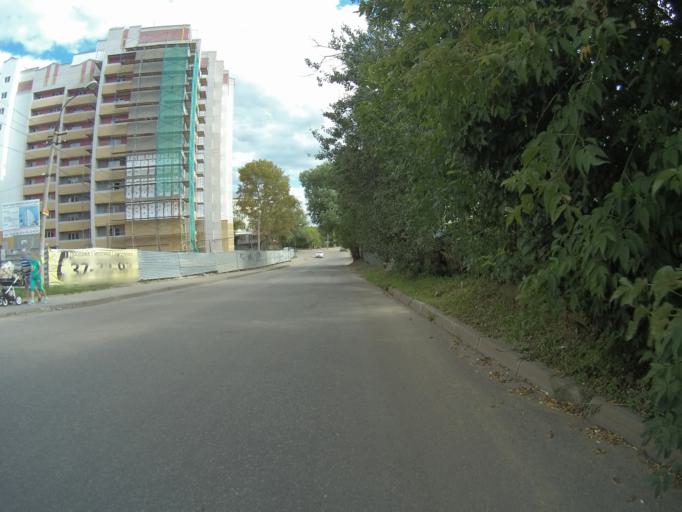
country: RU
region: Vladimir
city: Vladimir
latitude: 56.1158
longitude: 40.3734
